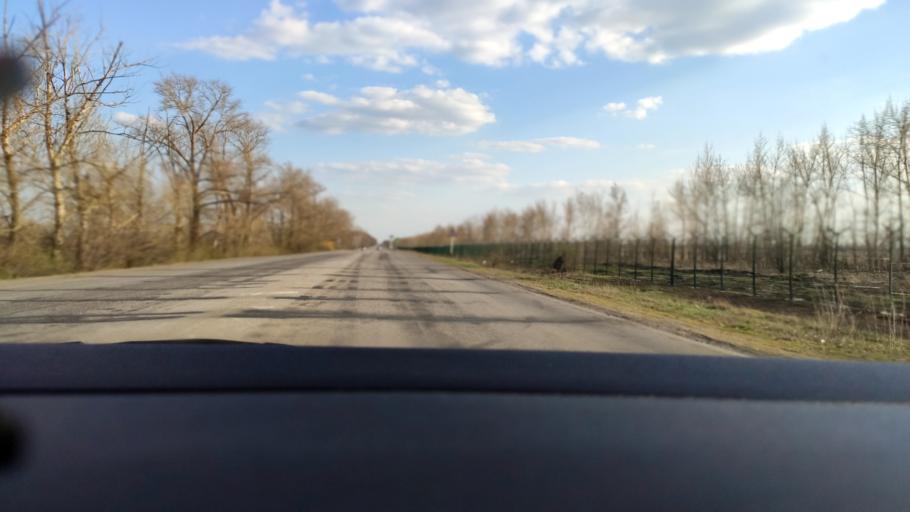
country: RU
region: Voronezj
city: Maslovka
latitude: 51.5340
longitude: 39.2909
